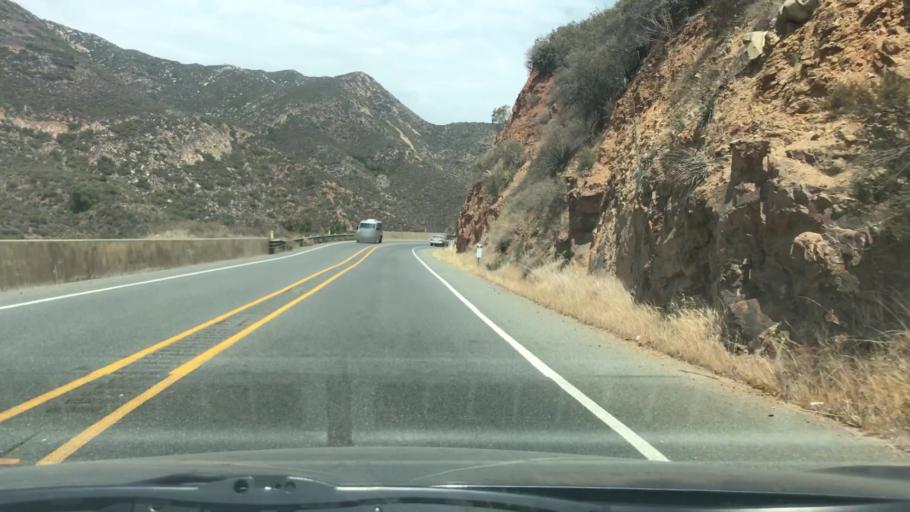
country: US
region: California
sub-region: Orange County
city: Coto De Caza
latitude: 33.5937
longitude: -117.4885
